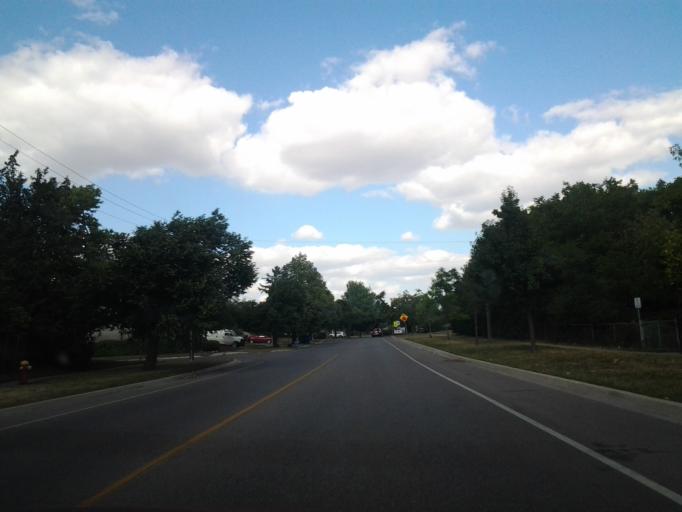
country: CA
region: Ontario
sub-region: Halton
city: Milton
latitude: 43.6431
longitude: -79.8895
